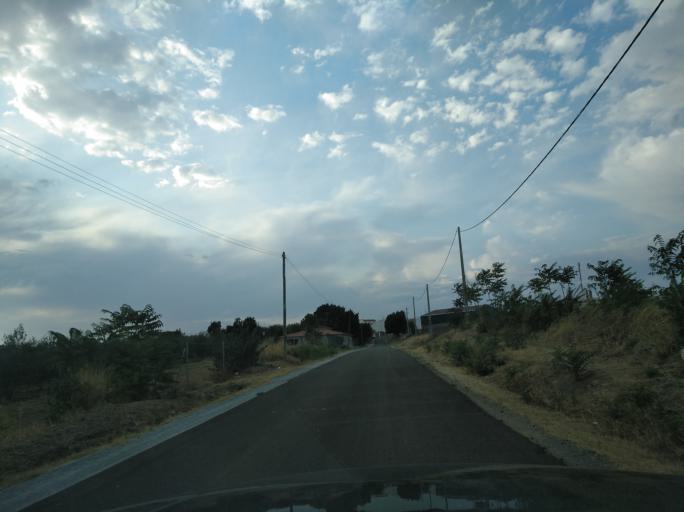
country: PT
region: Portalegre
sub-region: Campo Maior
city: Campo Maior
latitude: 39.0088
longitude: -7.0625
